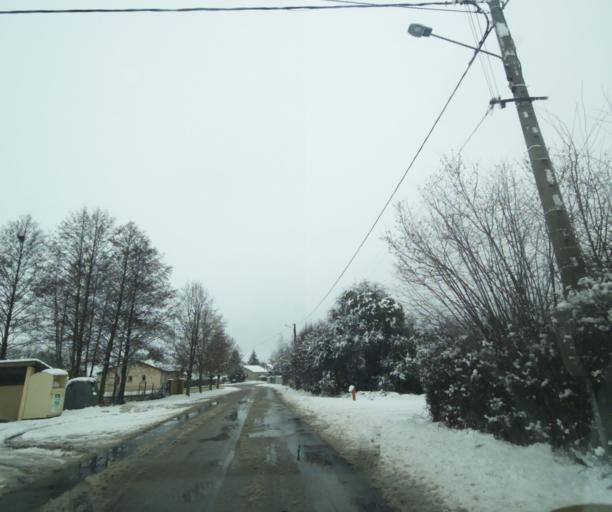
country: FR
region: Champagne-Ardenne
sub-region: Departement de la Haute-Marne
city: Montier-en-Der
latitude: 48.5060
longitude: 4.7878
